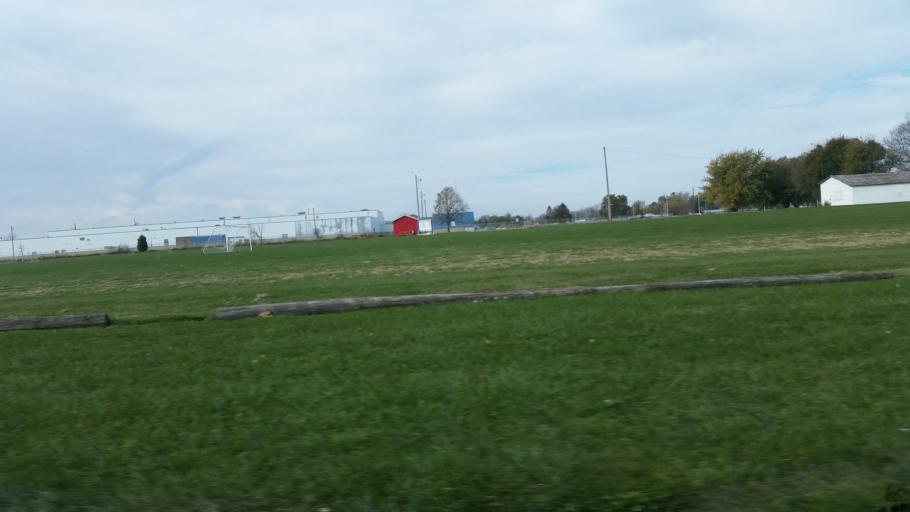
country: US
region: Indiana
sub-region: Howard County
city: Kokomo
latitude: 40.4679
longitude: -86.1555
